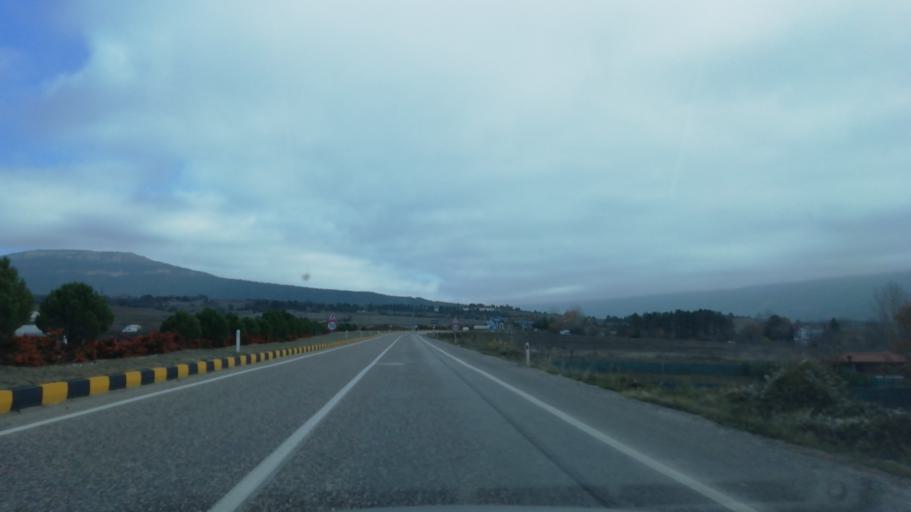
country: TR
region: Karabuk
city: Safranbolu
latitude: 41.2229
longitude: 32.7790
